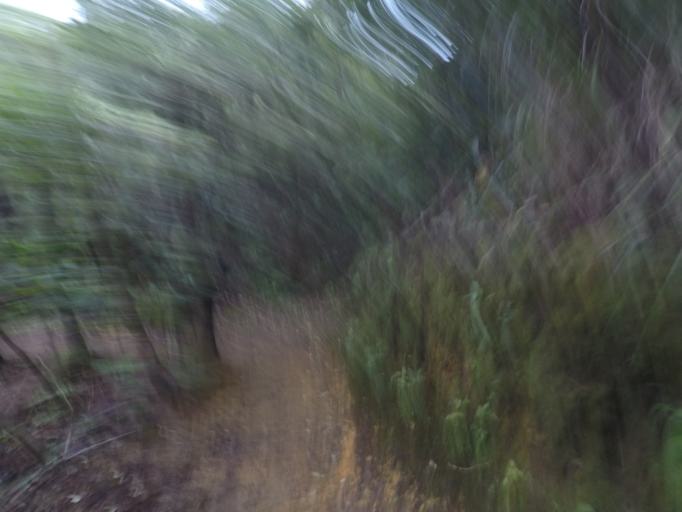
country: NZ
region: Bay of Plenty
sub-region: Western Bay of Plenty District
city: Waihi Beach
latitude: -37.3892
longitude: 175.9386
